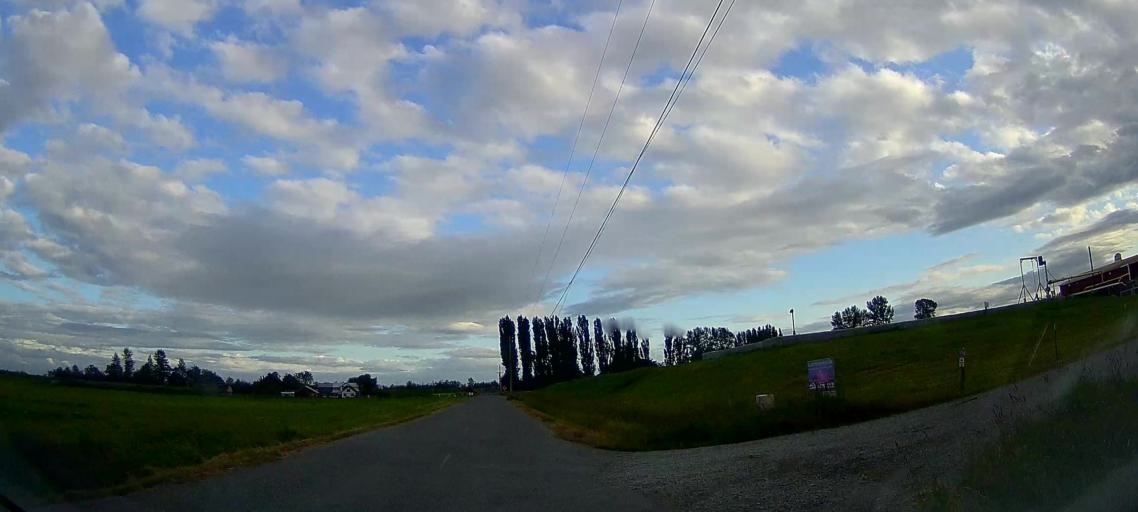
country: US
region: Washington
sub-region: Skagit County
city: Mount Vernon
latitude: 48.3722
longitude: -122.4005
